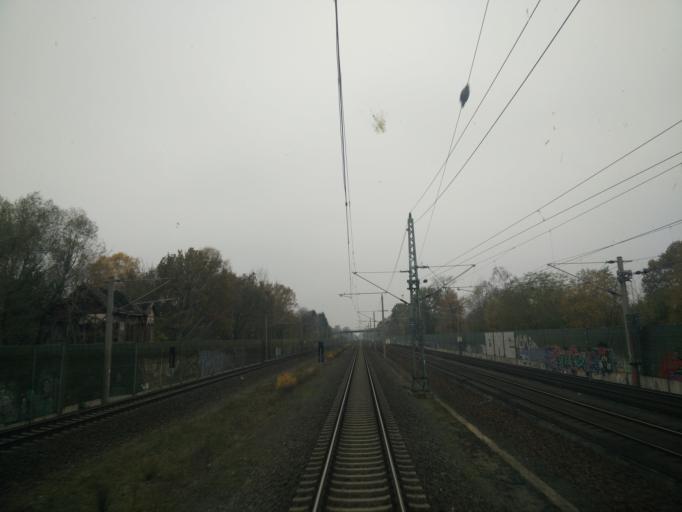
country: DE
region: Brandenburg
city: Dallgow-Doeberitz
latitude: 52.5429
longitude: 13.0701
